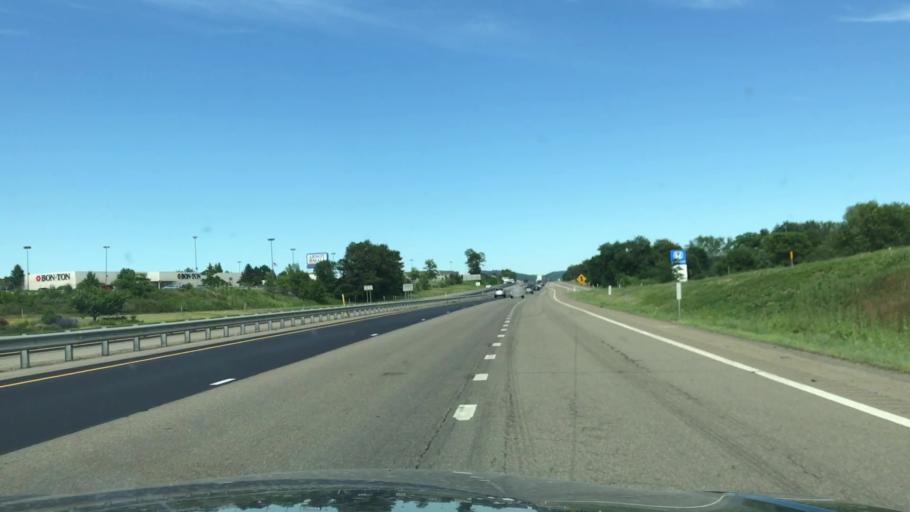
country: US
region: New York
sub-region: Chemung County
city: Horseheads
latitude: 42.1570
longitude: -76.8764
